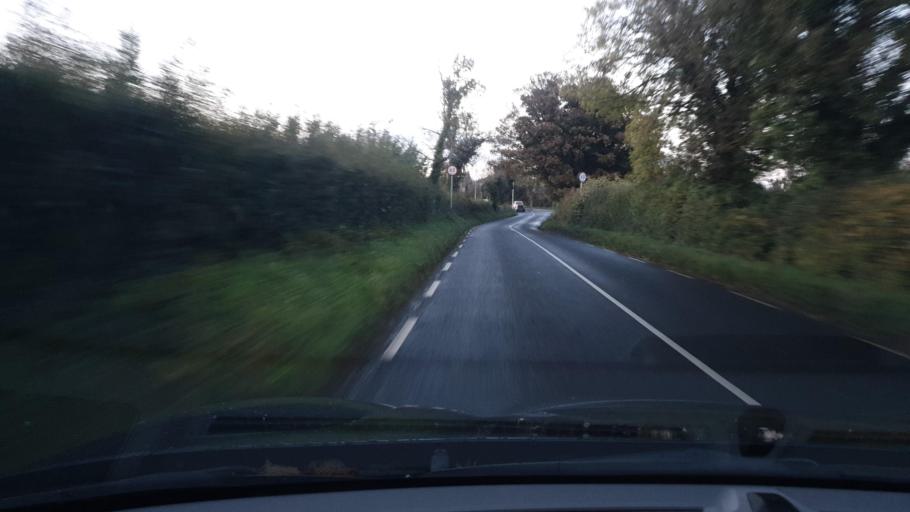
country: IE
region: Leinster
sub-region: An Mhi
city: Ratoath
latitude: 53.5022
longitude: -6.4436
